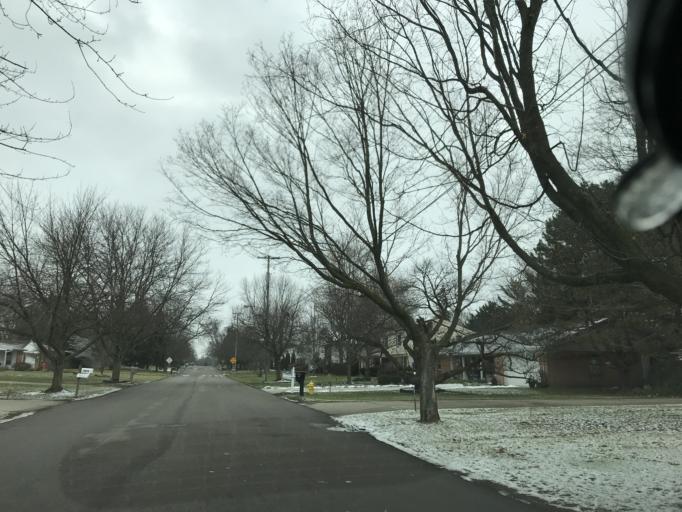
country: US
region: Michigan
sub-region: Kent County
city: East Grand Rapids
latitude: 42.9218
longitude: -85.5933
